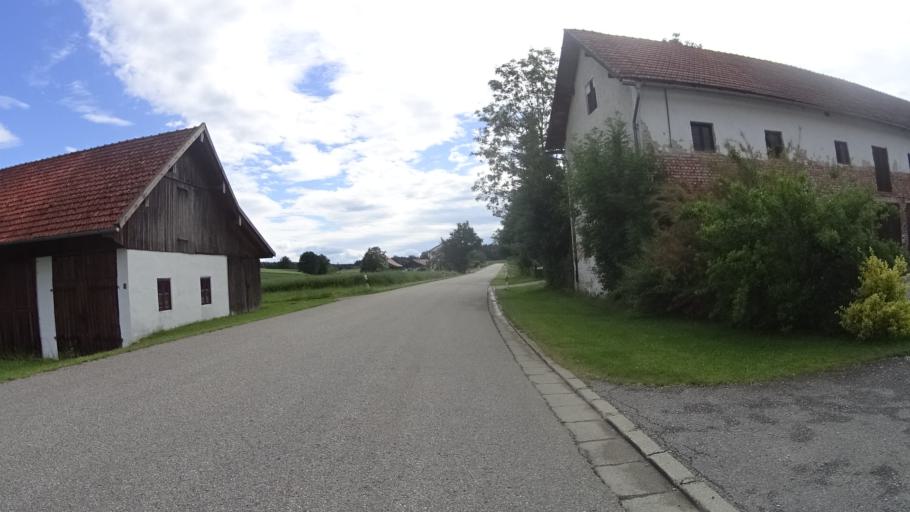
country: DE
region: Bavaria
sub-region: Lower Bavaria
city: Furth
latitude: 48.4003
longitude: 12.3630
